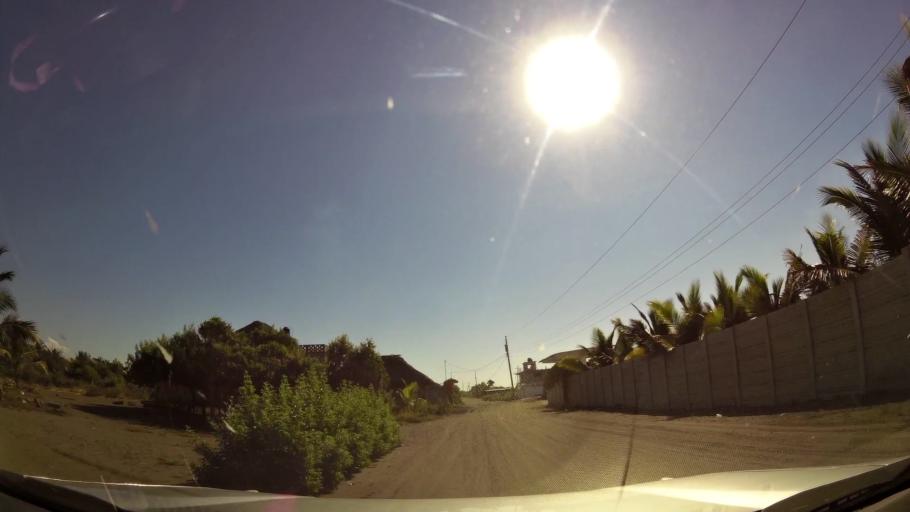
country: GT
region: Jutiapa
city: Pasaco
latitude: 13.8521
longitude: -90.3791
